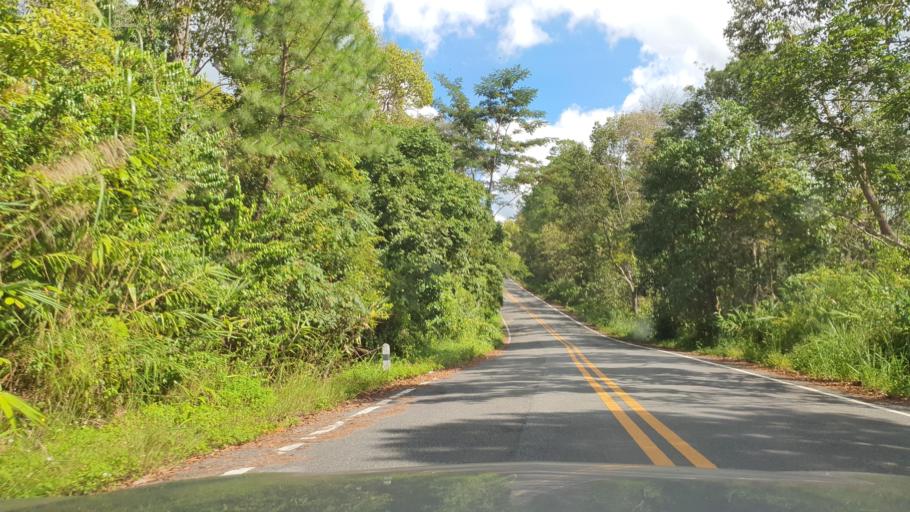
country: TH
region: Chiang Rai
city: Wiang Pa Pao
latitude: 19.3148
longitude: 99.3829
